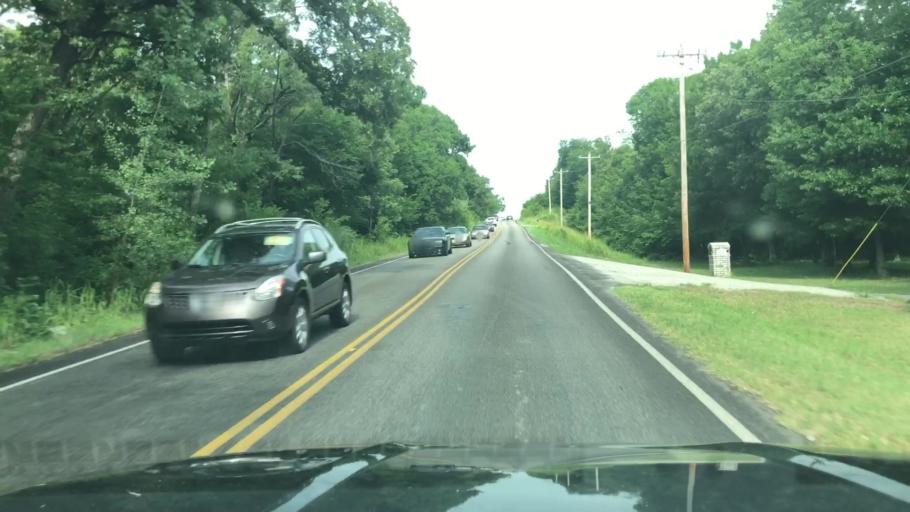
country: US
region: Oklahoma
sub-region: Tulsa County
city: Oakhurst
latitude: 36.0902
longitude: -96.1052
